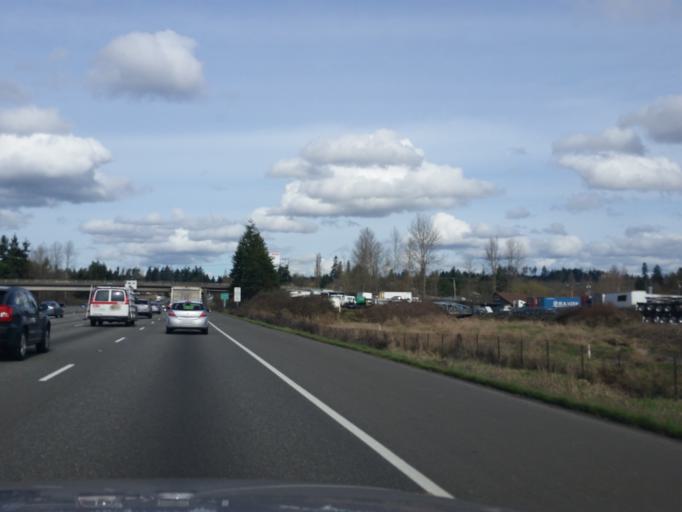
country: US
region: Washington
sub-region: Pierce County
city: Fife Heights
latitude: 47.2494
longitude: -122.3330
